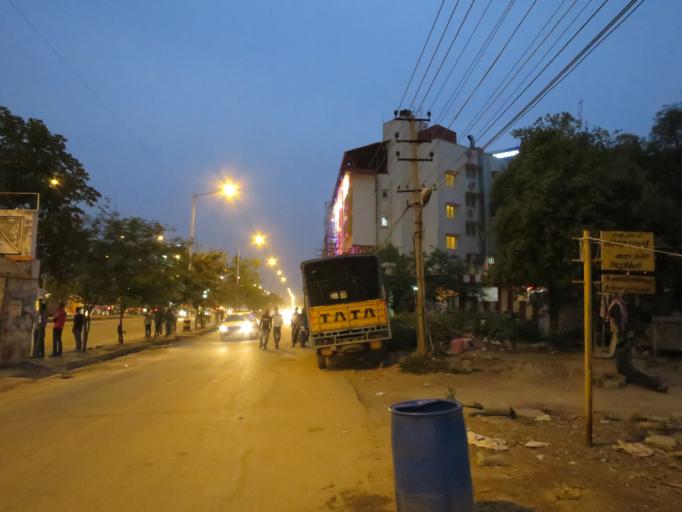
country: IN
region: Karnataka
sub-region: Bangalore Urban
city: Bangalore
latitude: 12.9782
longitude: 77.6957
